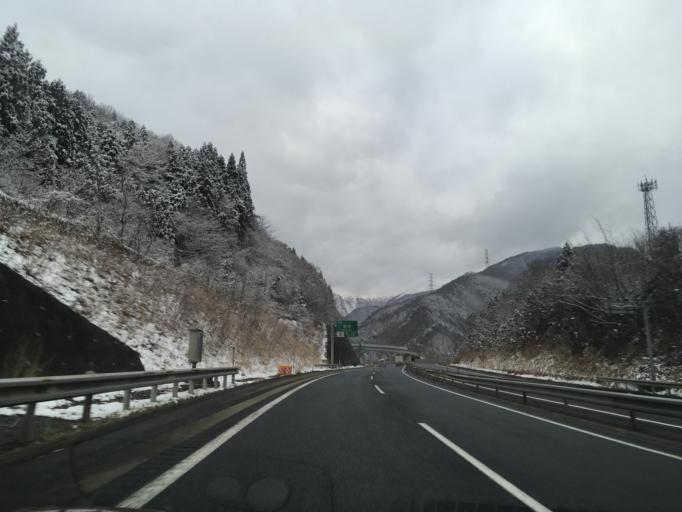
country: JP
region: Yamagata
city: Yamagata-shi
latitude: 38.2211
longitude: 140.5141
